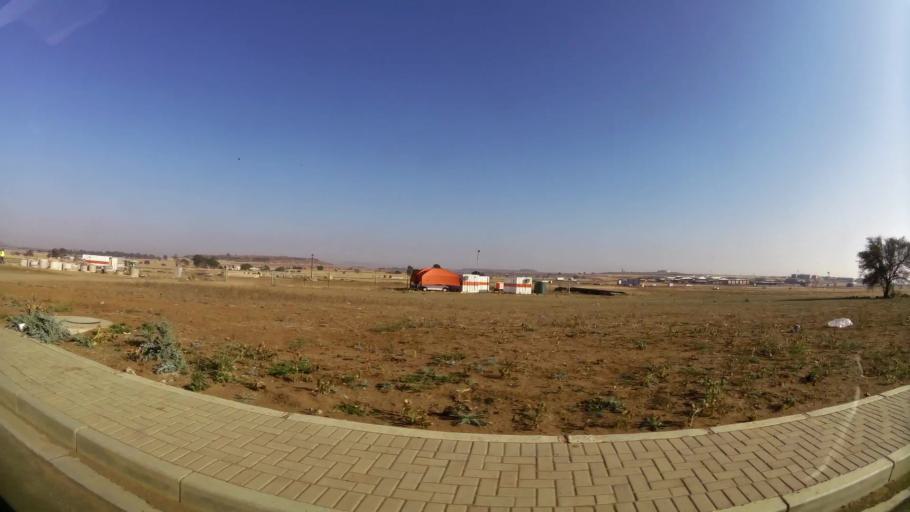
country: ZA
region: Orange Free State
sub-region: Mangaung Metropolitan Municipality
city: Bloemfontein
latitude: -29.1951
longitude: 26.2178
